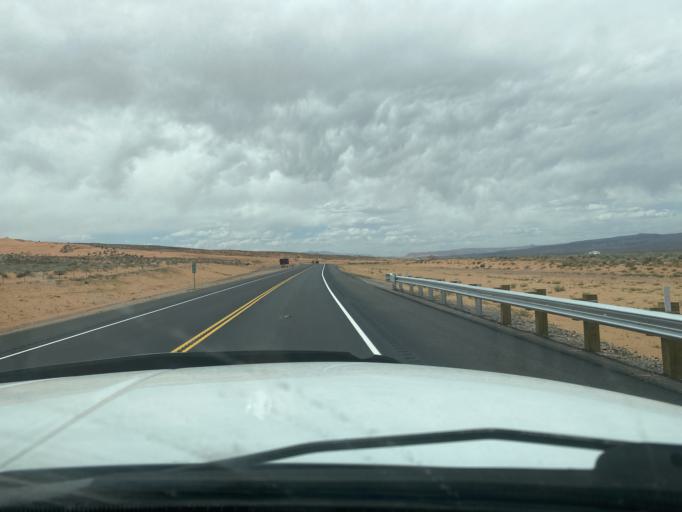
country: US
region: Utah
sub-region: Washington County
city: Hurricane
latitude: 37.0982
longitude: -113.3681
